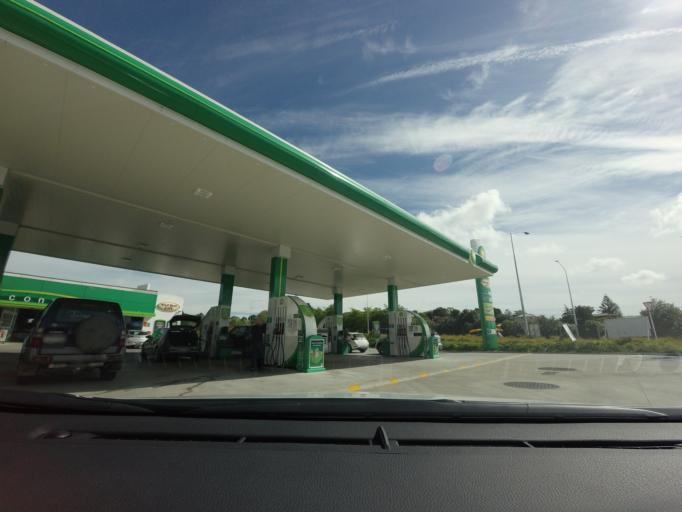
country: NZ
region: Auckland
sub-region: Auckland
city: Warkworth
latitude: -36.4086
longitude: 174.6594
